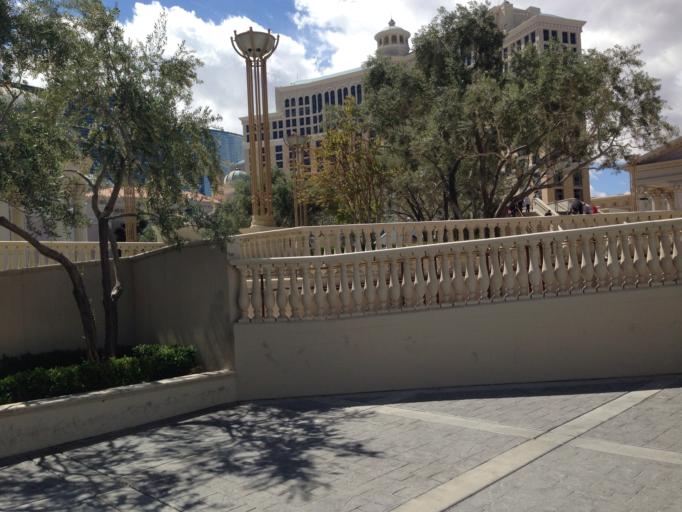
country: US
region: Nevada
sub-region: Clark County
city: Paradise
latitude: 36.1153
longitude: -115.1732
